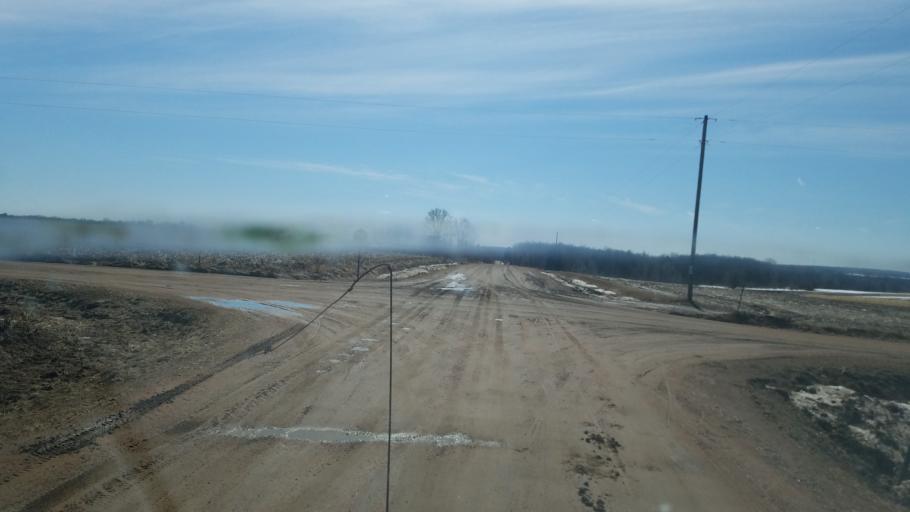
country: US
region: Wisconsin
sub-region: Clark County
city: Loyal
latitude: 44.6111
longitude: -90.4271
